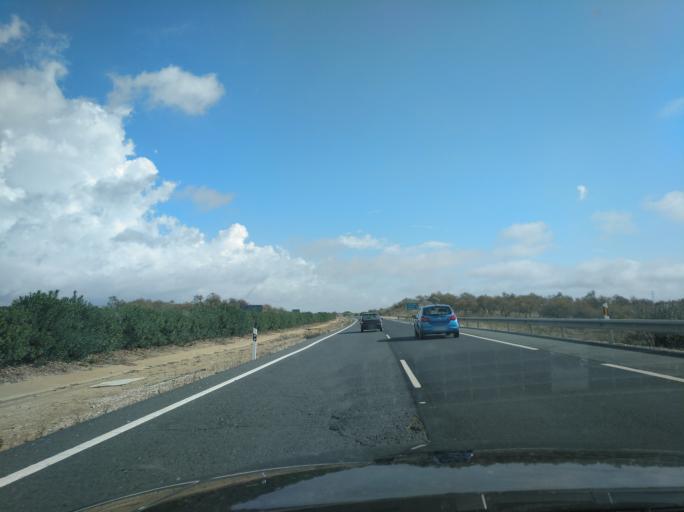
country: ES
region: Andalusia
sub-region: Provincia de Huelva
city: Aljaraque
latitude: 37.3239
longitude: -7.0609
